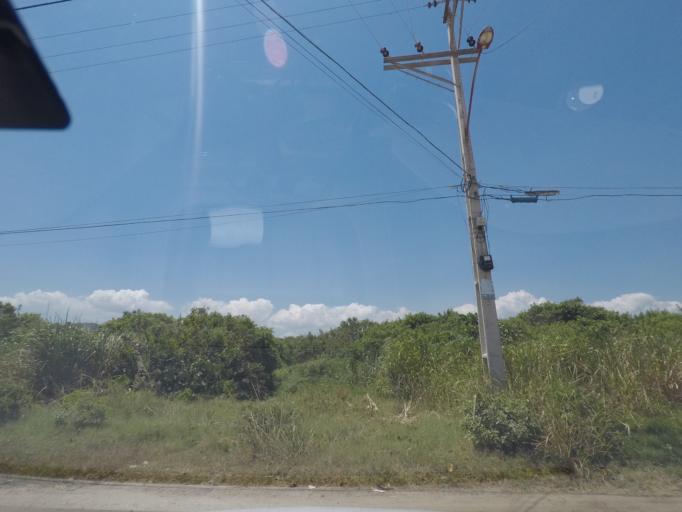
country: BR
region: Rio de Janeiro
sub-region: Marica
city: Marica
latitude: -22.9687
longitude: -42.9684
